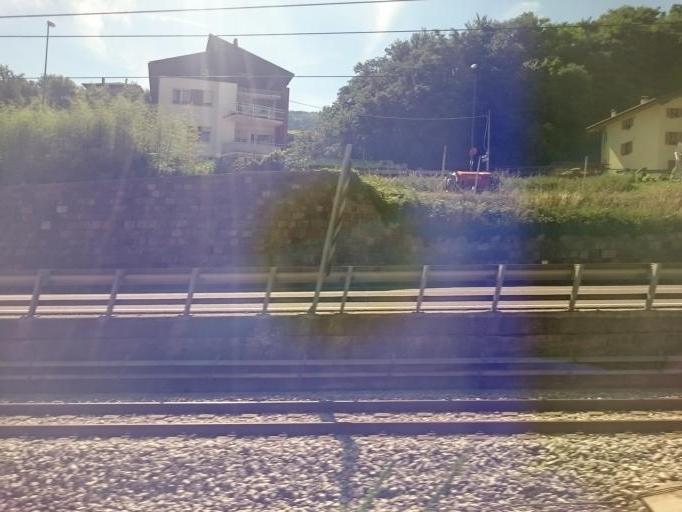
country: IT
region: Trentino-Alto Adige
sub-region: Provincia di Trento
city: Nave San Rocco
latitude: 46.1616
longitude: 11.1089
